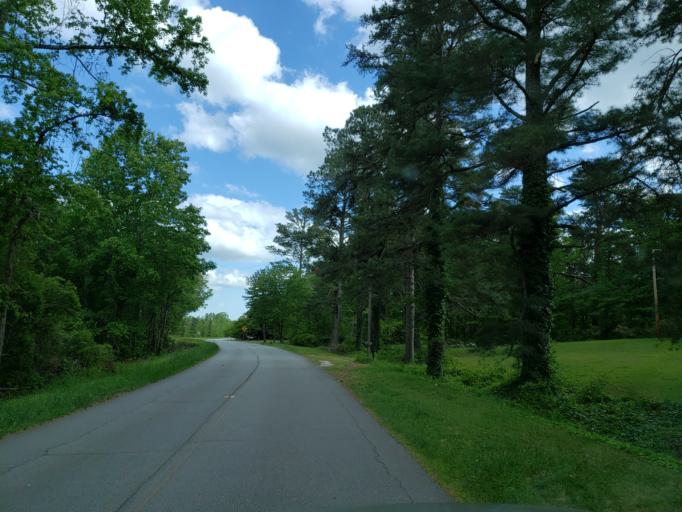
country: US
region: Georgia
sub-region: Carroll County
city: Mount Zion
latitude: 33.6394
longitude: -85.2784
